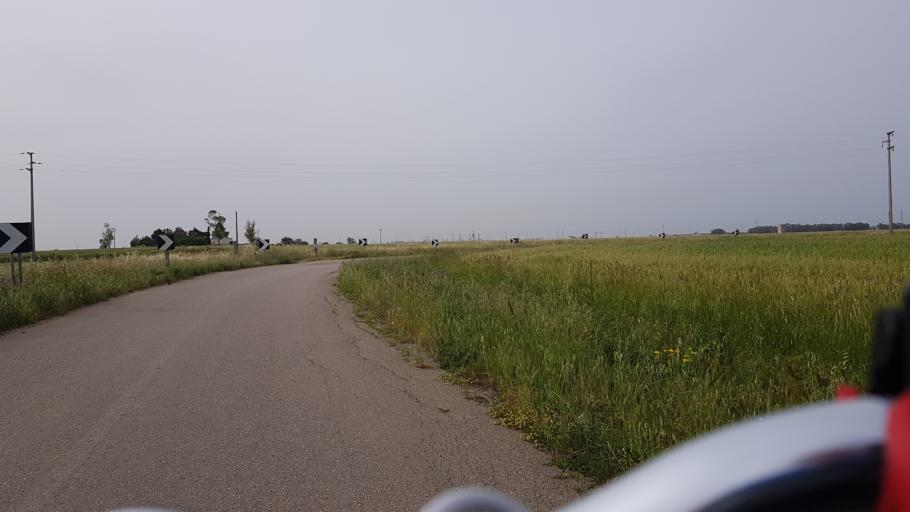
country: IT
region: Apulia
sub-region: Provincia di Brindisi
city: La Rosa
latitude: 40.5738
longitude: 18.0137
